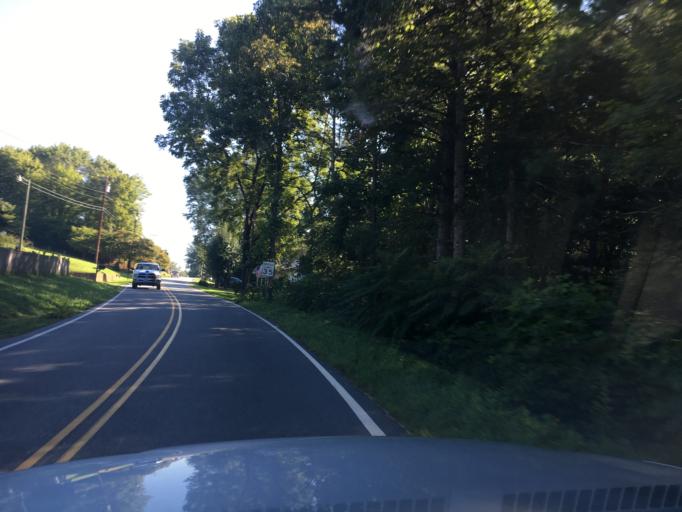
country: US
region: North Carolina
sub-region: McDowell County
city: West Marion
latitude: 35.6715
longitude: -82.0259
